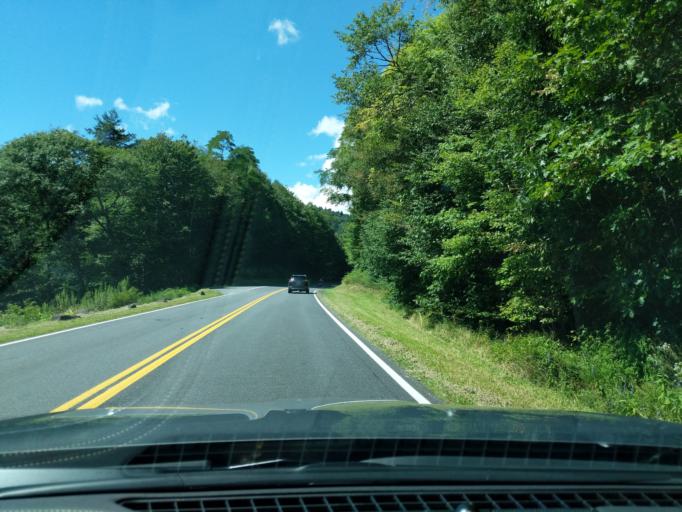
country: US
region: Tennessee
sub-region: Sevier County
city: Gatlinburg
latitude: 35.5989
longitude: -83.4221
